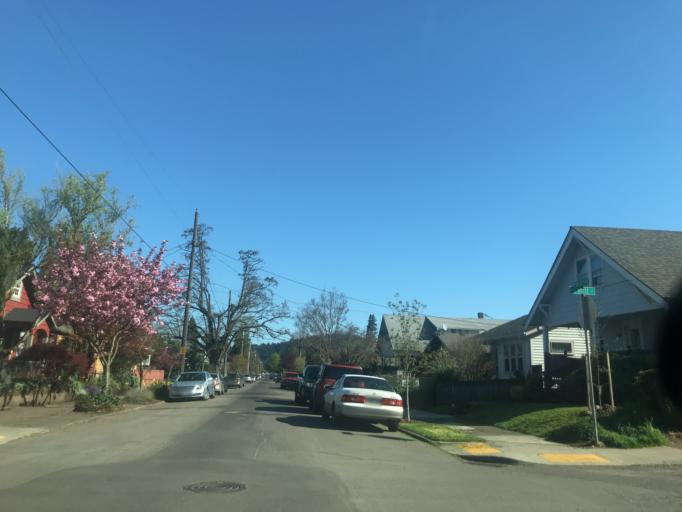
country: US
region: Oregon
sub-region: Multnomah County
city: Lents
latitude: 45.4920
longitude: -122.5963
